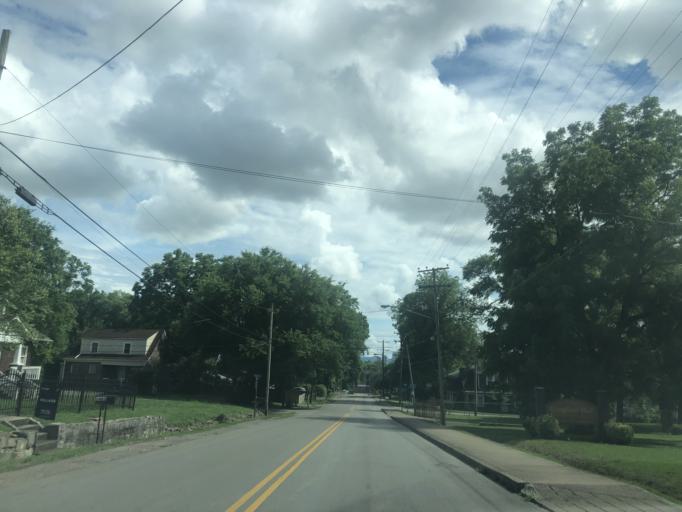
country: US
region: Tennessee
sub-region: Davidson County
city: Nashville
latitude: 36.1976
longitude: -86.7670
